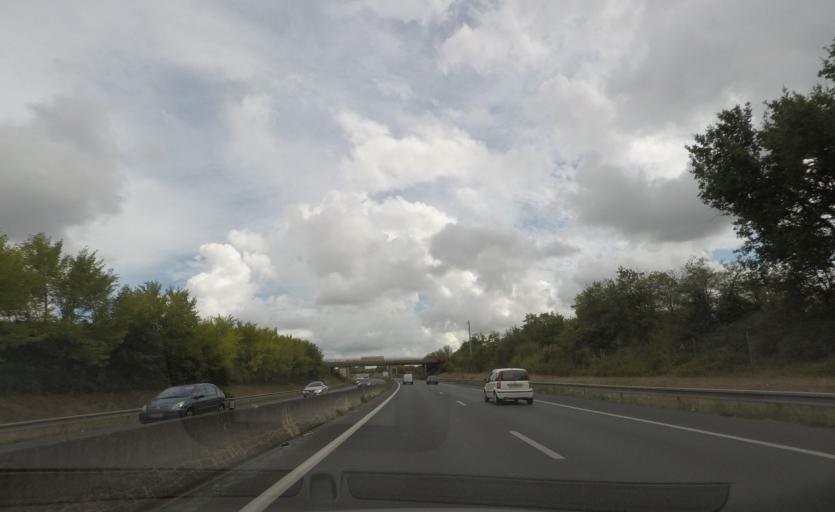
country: FR
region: Pays de la Loire
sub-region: Departement de Maine-et-Loire
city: Trelaze
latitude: 47.4776
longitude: -0.5016
